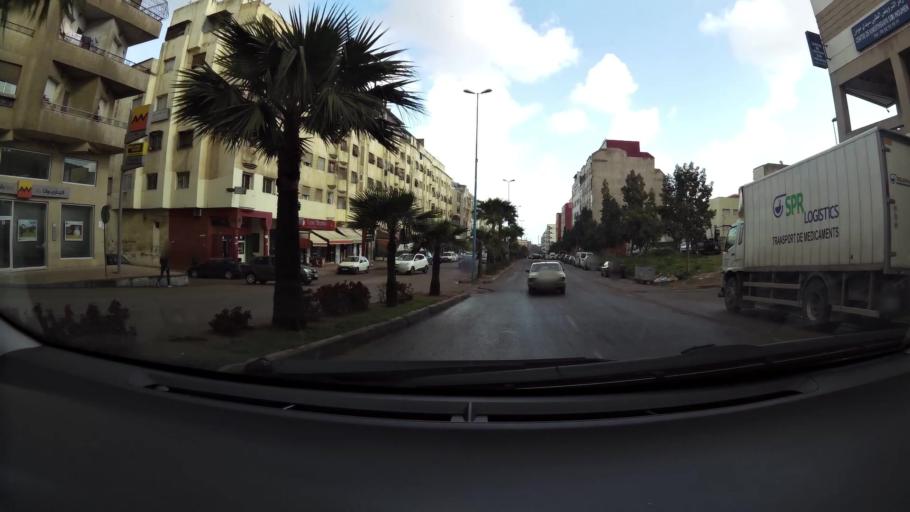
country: MA
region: Grand Casablanca
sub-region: Mediouna
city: Tit Mellil
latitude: 33.5816
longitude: -7.5243
